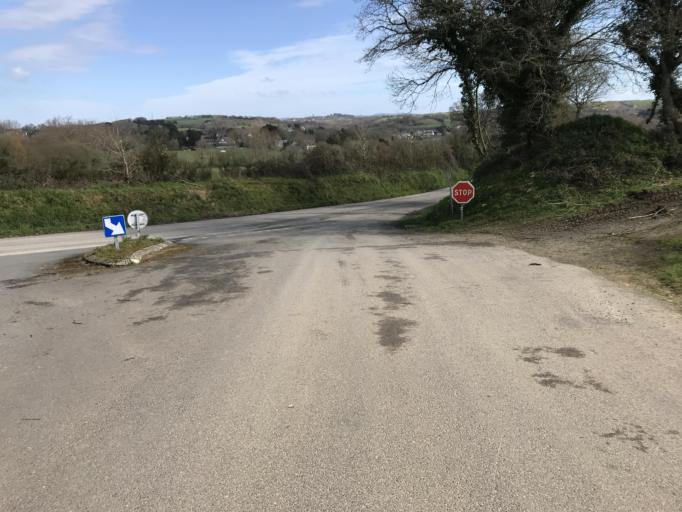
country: FR
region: Brittany
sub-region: Departement du Finistere
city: Daoulas
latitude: 48.3617
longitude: -4.2764
